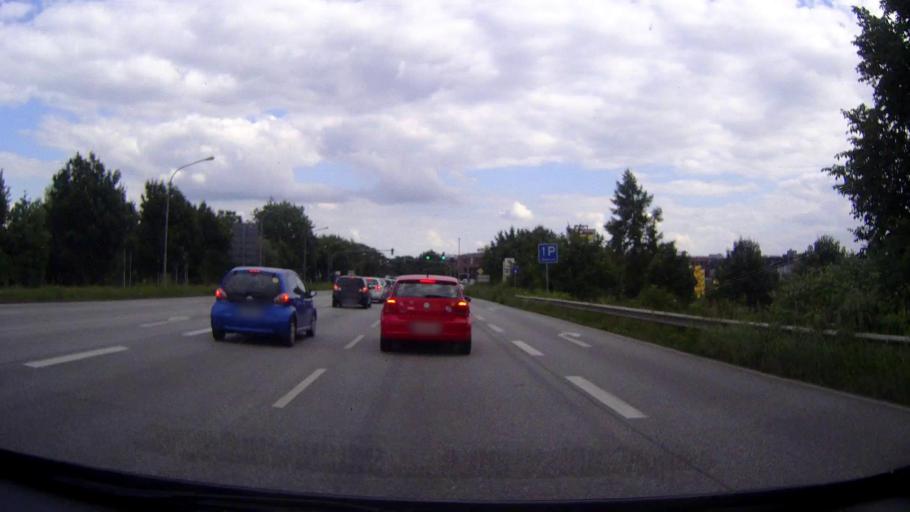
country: DE
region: Schleswig-Holstein
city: Stockelsdorf
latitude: 53.8616
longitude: 10.6257
